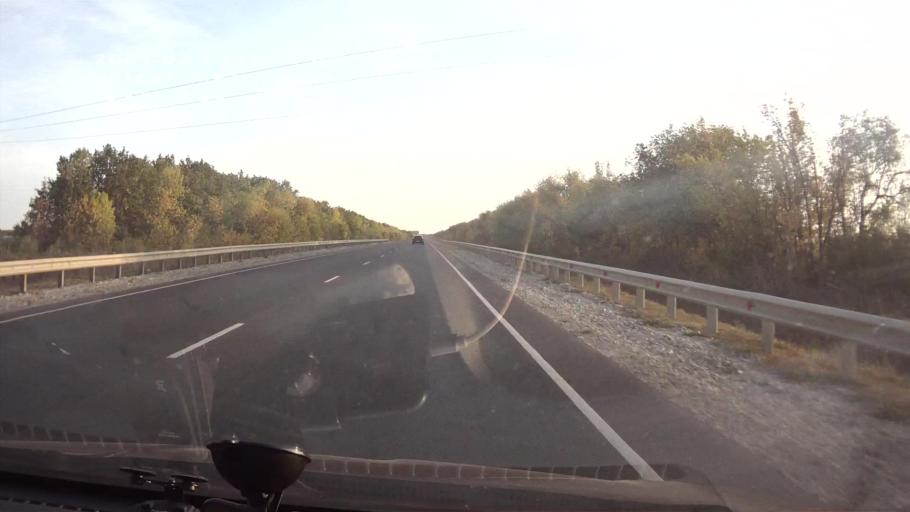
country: RU
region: Saratov
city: Krasnoarmeysk
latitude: 51.0915
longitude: 45.6467
